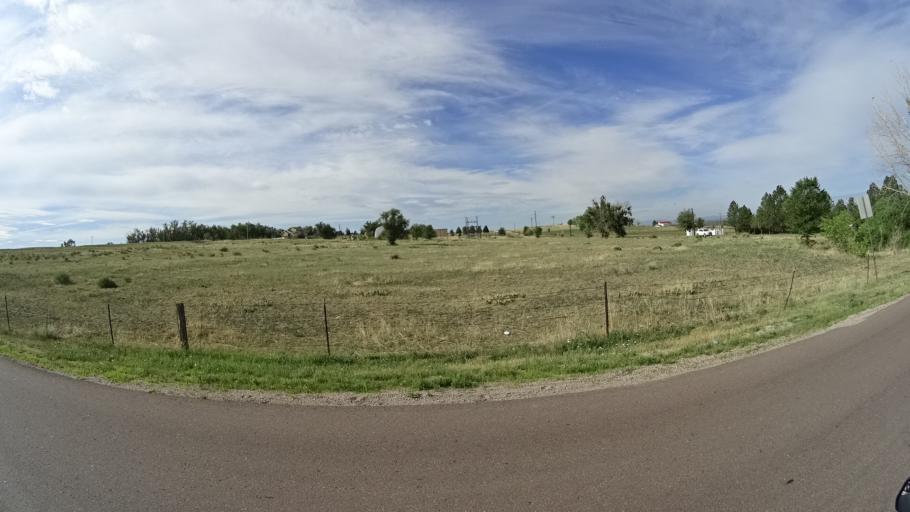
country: US
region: Colorado
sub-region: El Paso County
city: Fountain
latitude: 38.6865
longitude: -104.6775
